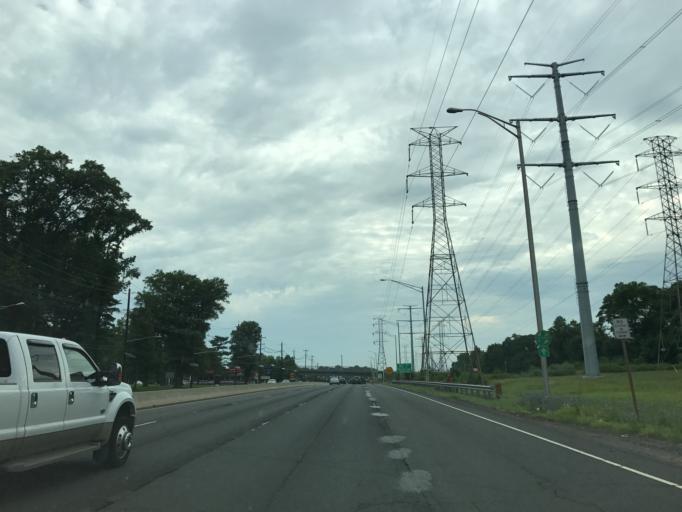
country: US
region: New Jersey
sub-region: Middlesex County
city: Fords
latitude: 40.5407
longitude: -74.3373
